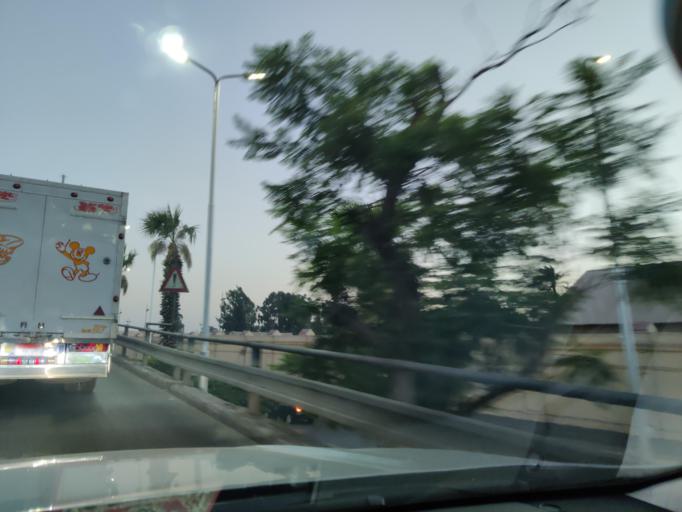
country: EG
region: Muhafazat al Qahirah
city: Cairo
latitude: 30.1007
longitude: 31.3056
